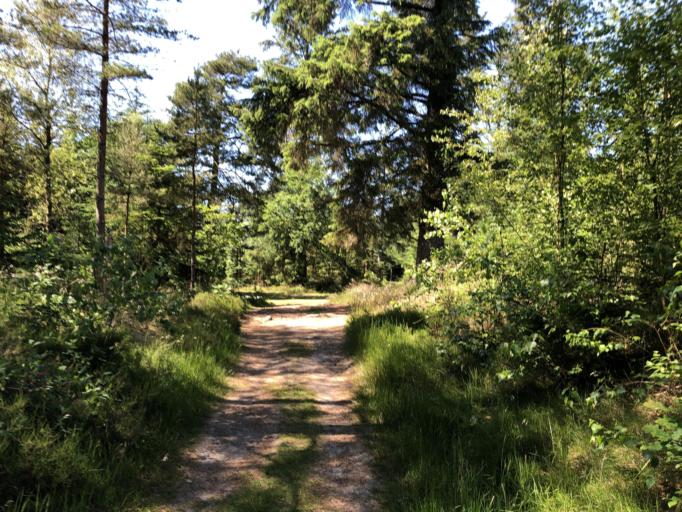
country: DK
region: South Denmark
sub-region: Varde Kommune
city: Oksbol
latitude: 55.7504
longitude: 8.2387
